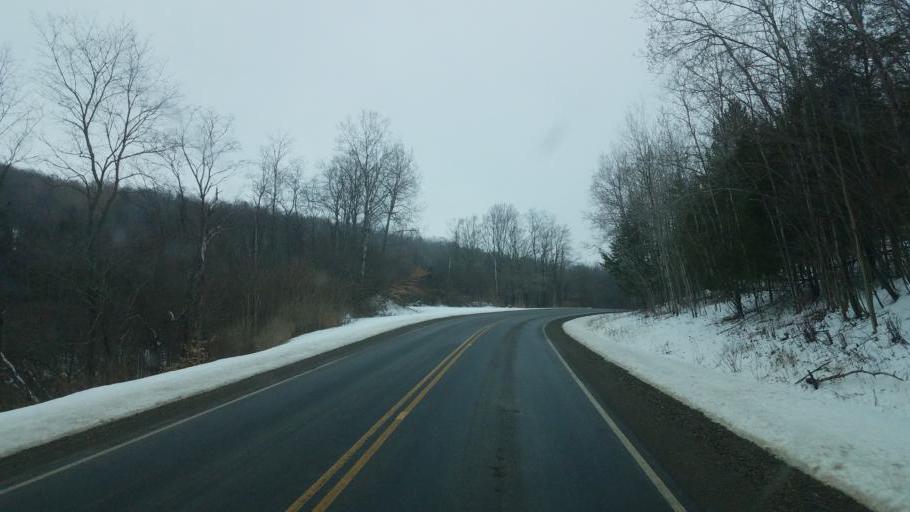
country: US
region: New York
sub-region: Allegany County
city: Andover
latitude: 42.0228
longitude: -77.7516
